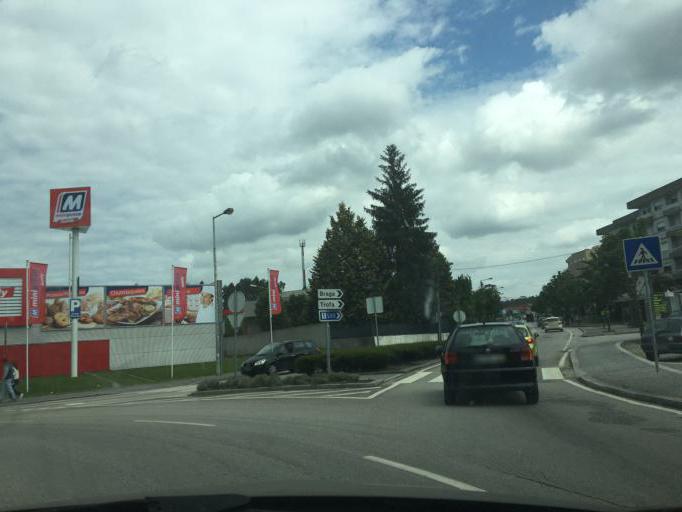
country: PT
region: Porto
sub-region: Maia
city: Anta
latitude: 41.2668
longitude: -8.6118
